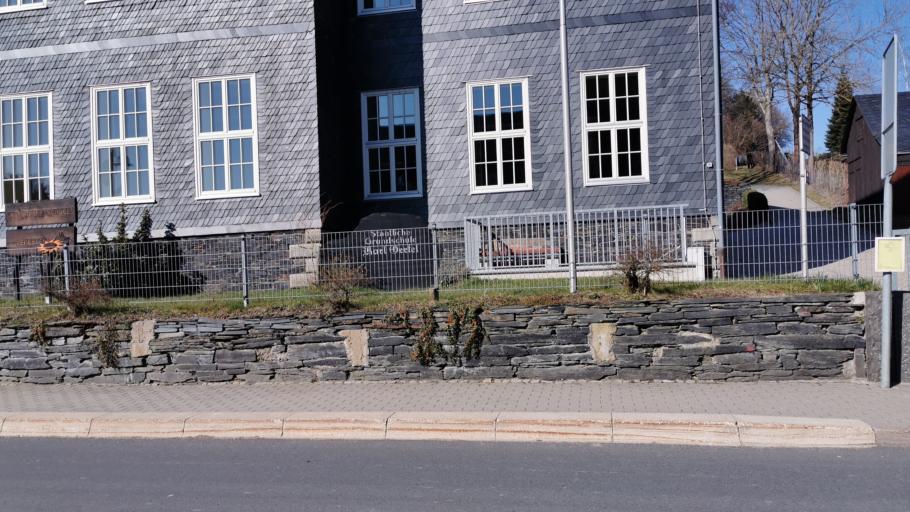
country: DE
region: Bavaria
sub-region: Upper Franconia
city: Ludwigsstadt
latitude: 50.4770
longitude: 11.4438
